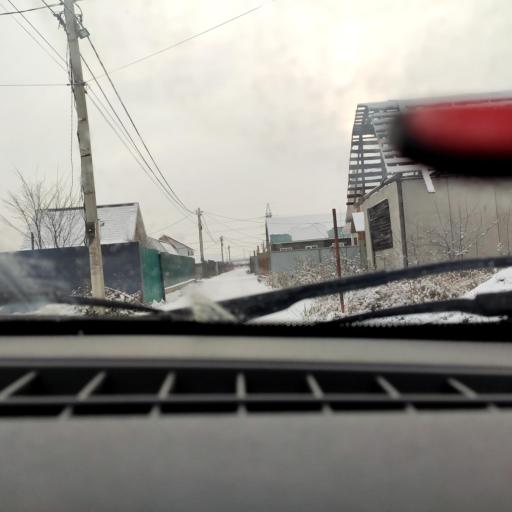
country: RU
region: Bashkortostan
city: Ufa
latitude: 54.6279
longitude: 55.8862
